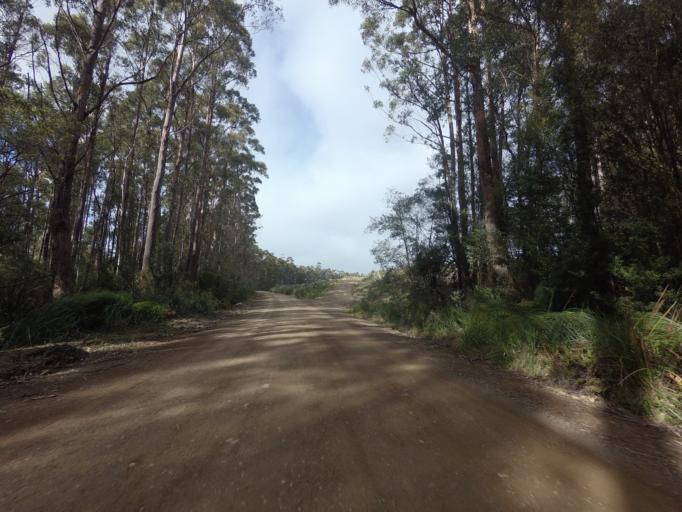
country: AU
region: Tasmania
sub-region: Huon Valley
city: Geeveston
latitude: -43.4854
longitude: 146.8913
